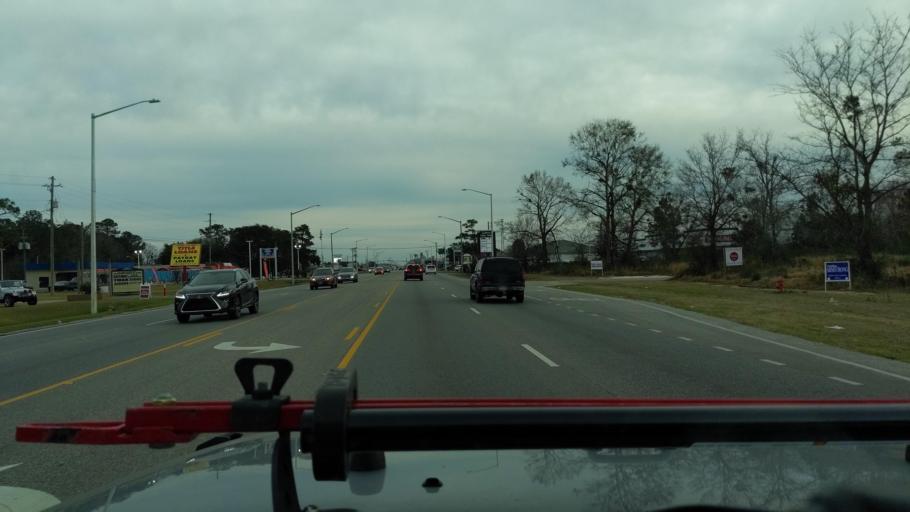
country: US
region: Alabama
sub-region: Baldwin County
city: Foley
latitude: 30.3867
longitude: -87.6834
